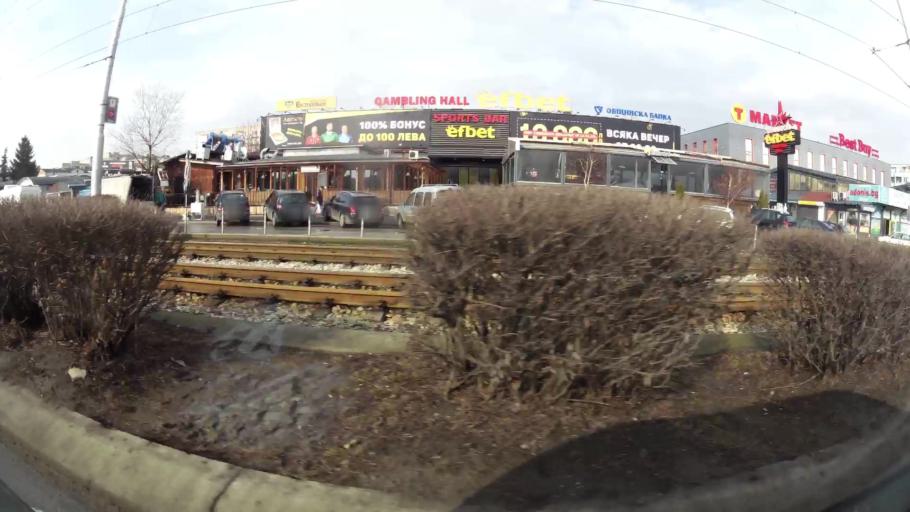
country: BG
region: Sofiya
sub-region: Obshtina Bozhurishte
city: Bozhurishte
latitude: 42.7172
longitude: 23.2525
